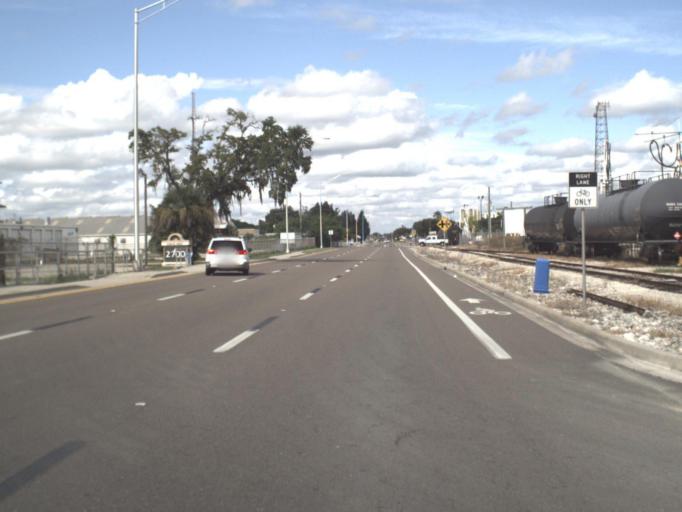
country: US
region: Florida
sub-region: Lee County
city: Fort Myers
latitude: 26.6273
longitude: -81.8601
